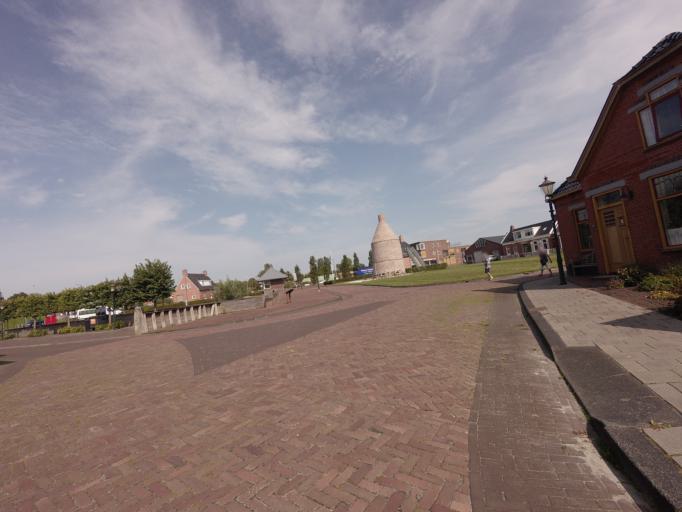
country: NL
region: Groningen
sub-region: Gemeente De Marne
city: Ulrum
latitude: 53.3387
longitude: 6.3004
